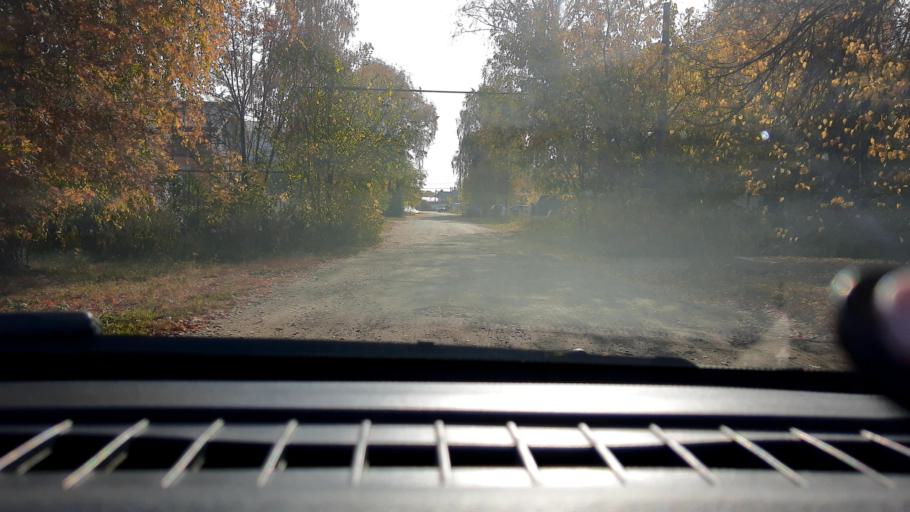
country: RU
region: Nizjnij Novgorod
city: Gorbatovka
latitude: 56.2116
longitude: 43.7550
